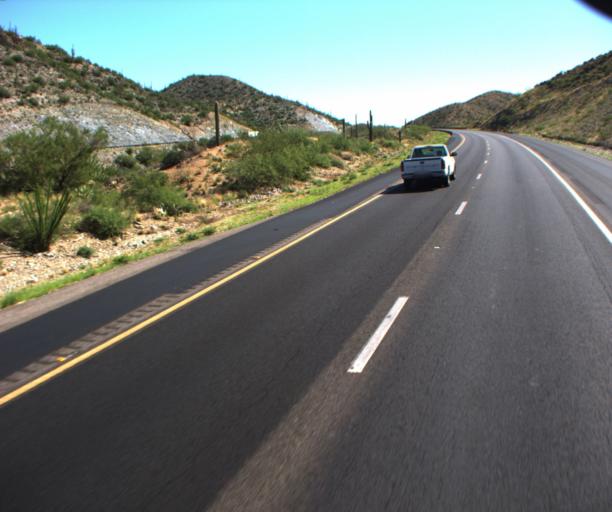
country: US
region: Arizona
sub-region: Pinal County
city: Gold Camp
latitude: 33.2715
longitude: -111.2394
